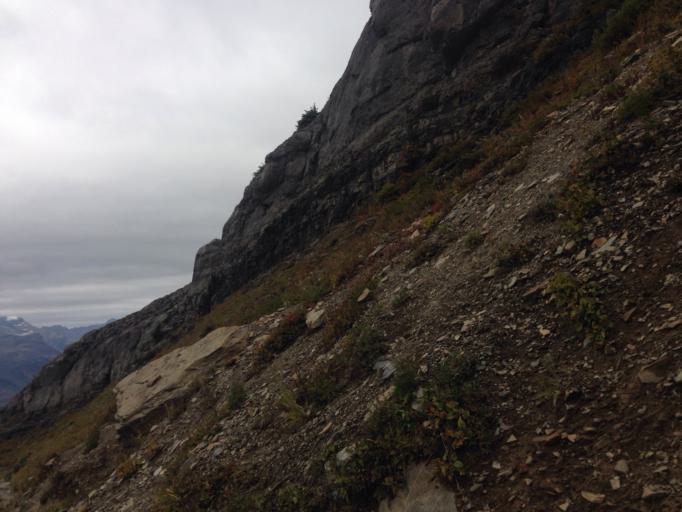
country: US
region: Montana
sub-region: Flathead County
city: Columbia Falls
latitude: 48.7444
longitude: -113.7347
